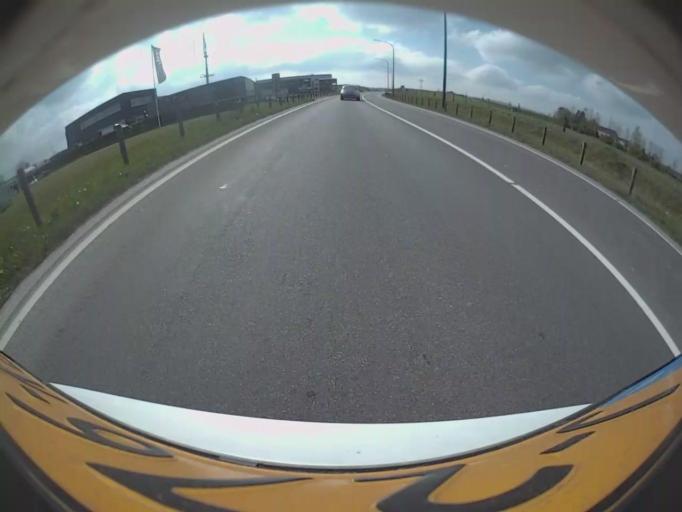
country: BE
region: Wallonia
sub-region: Province du Luxembourg
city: Marche-en-Famenne
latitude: 50.2407
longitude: 5.3381
